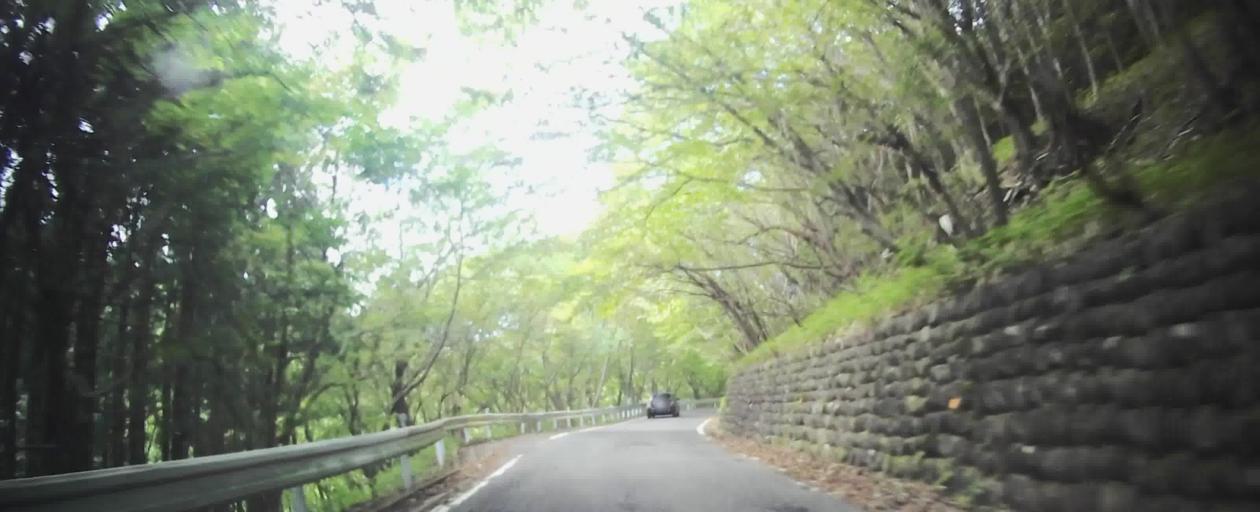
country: JP
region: Gunma
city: Shibukawa
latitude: 36.4604
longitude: 138.8937
